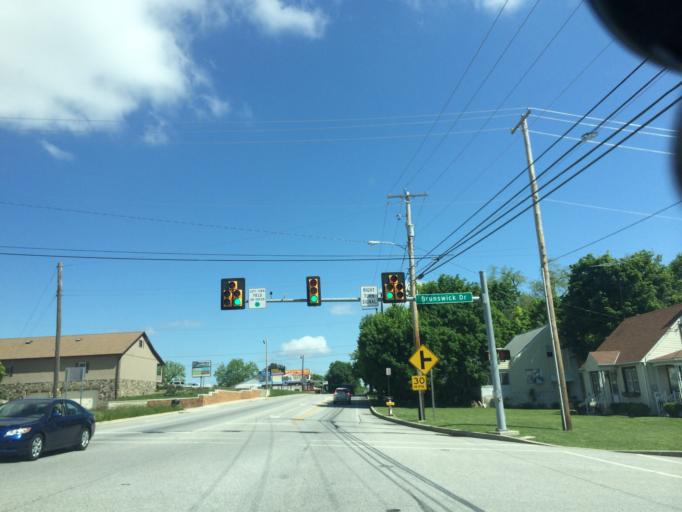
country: US
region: Pennsylvania
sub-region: York County
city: Parkville
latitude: 39.7632
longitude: -76.9600
